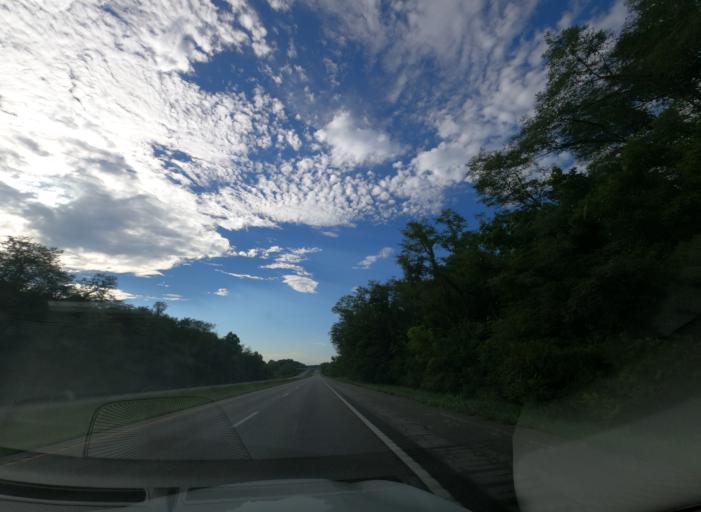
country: US
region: Missouri
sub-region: Jefferson County
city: Crystal City
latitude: 38.1353
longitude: -90.3226
